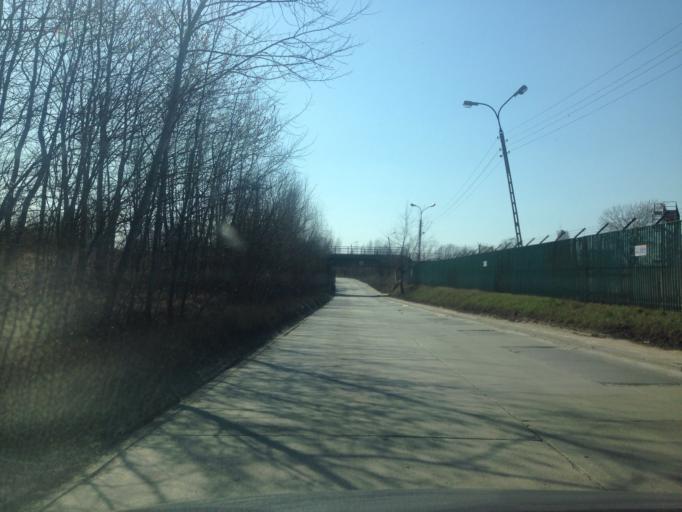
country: PL
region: Masovian Voivodeship
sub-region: Warszawa
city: Wilanow
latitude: 52.1833
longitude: 21.0916
